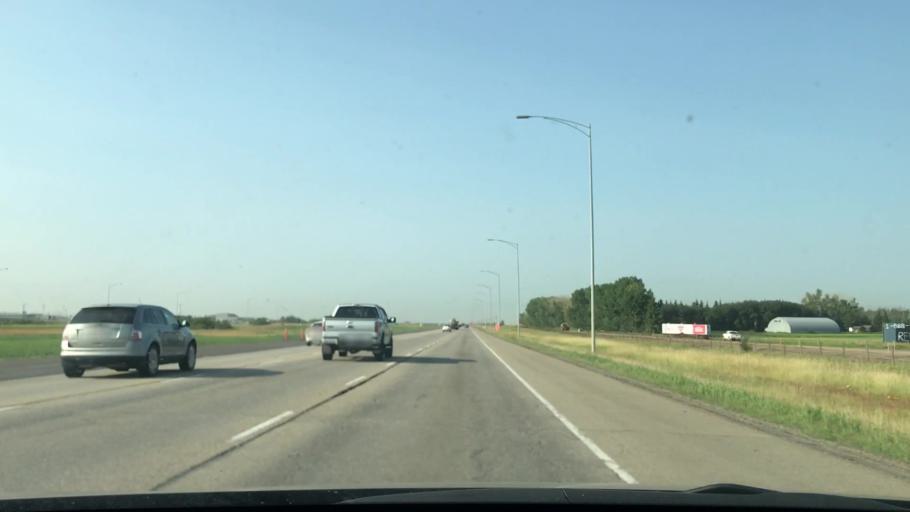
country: CA
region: Alberta
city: Leduc
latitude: 53.3674
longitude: -113.5322
